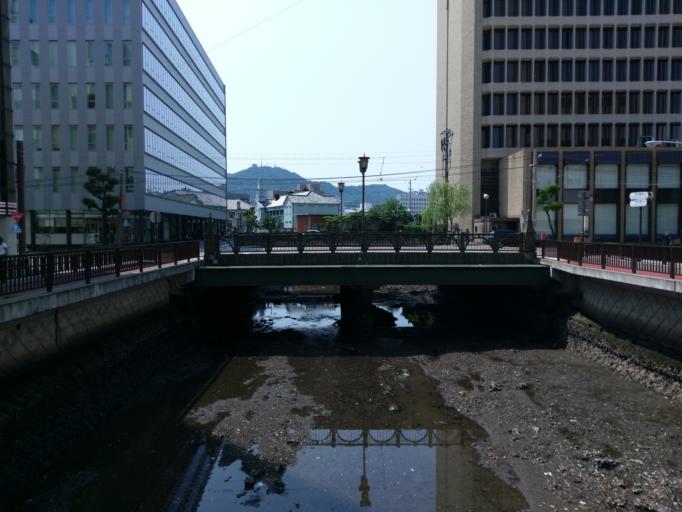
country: JP
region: Nagasaki
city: Nagasaki-shi
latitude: 32.7425
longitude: 129.8752
